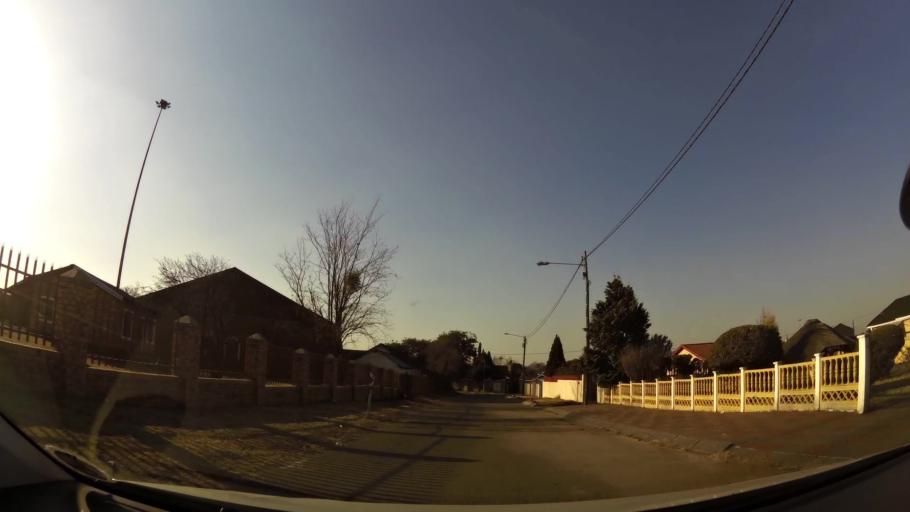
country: ZA
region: Gauteng
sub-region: City of Johannesburg Metropolitan Municipality
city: Soweto
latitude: -26.2647
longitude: 27.8771
